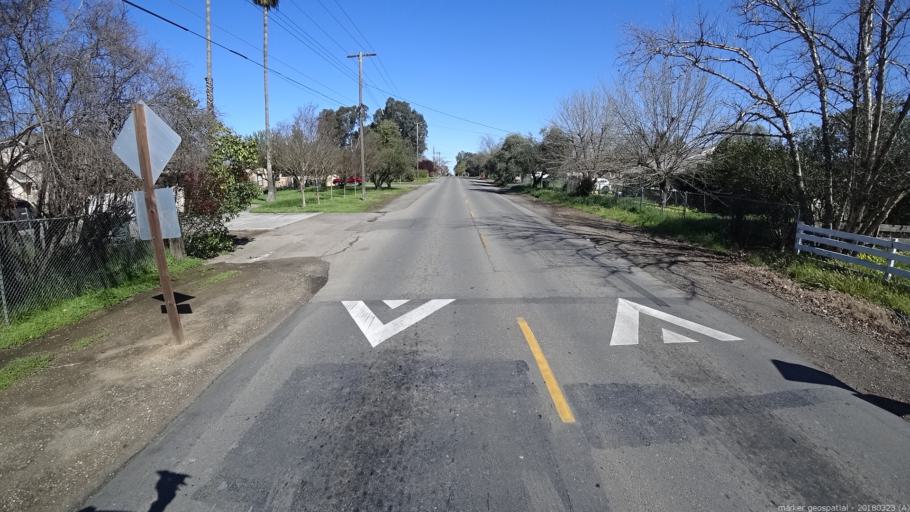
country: US
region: California
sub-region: Sacramento County
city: Rio Linda
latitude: 38.6963
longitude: -121.4384
